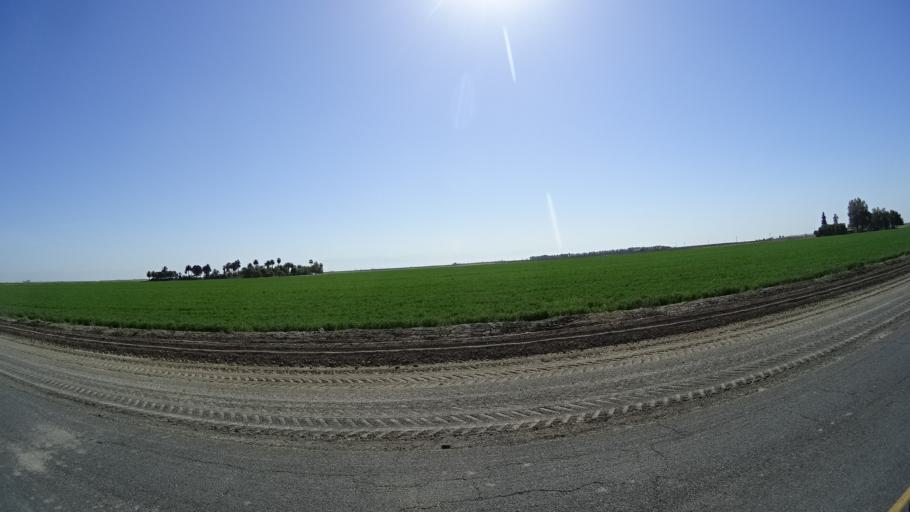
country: US
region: California
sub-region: Kings County
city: Home Garden
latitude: 36.2305
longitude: -119.5473
